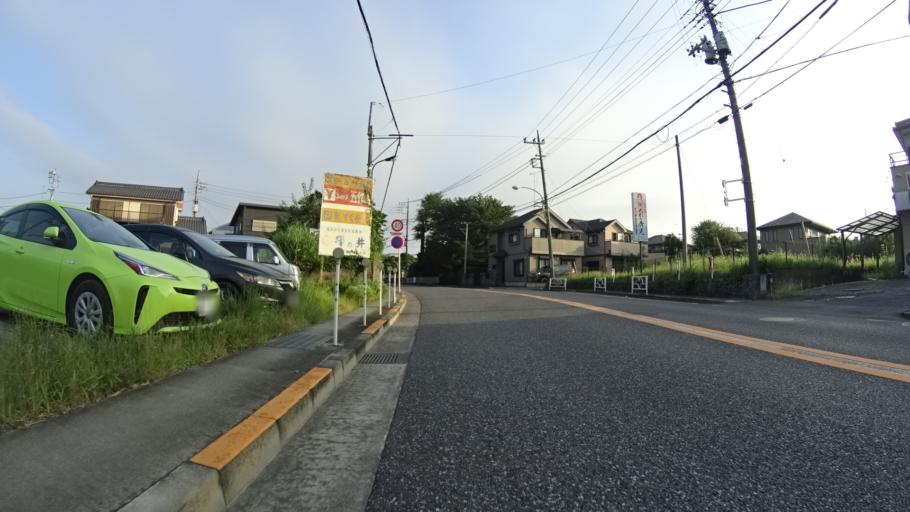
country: JP
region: Tokyo
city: Fussa
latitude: 35.7667
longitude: 139.3001
